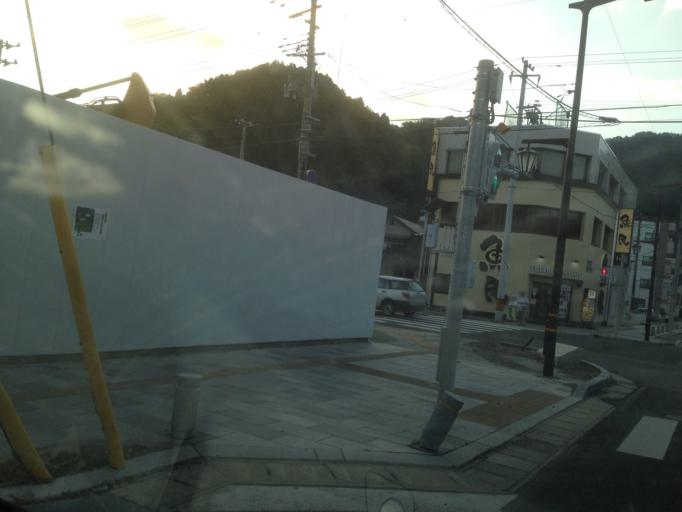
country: JP
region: Iwate
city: Kamaishi
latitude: 39.2736
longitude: 141.8817
